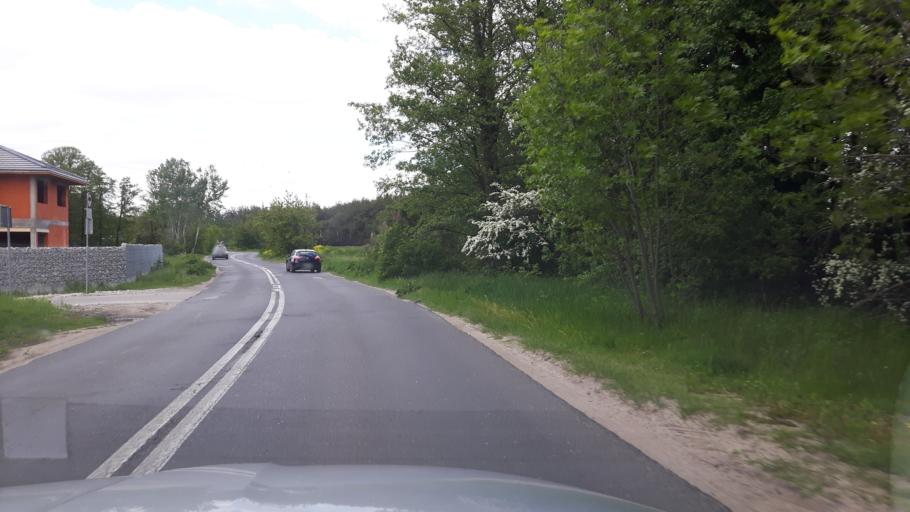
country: PL
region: Masovian Voivodeship
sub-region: Powiat legionowski
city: Stanislawow Pierwszy
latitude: 52.3375
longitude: 21.0540
